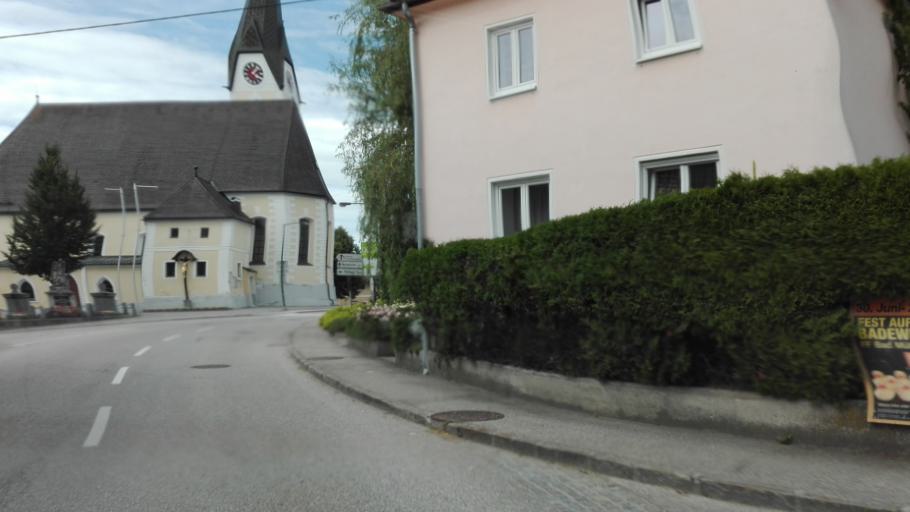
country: AT
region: Upper Austria
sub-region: Politischer Bezirk Grieskirchen
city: Grieskirchen
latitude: 48.2877
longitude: 13.8316
